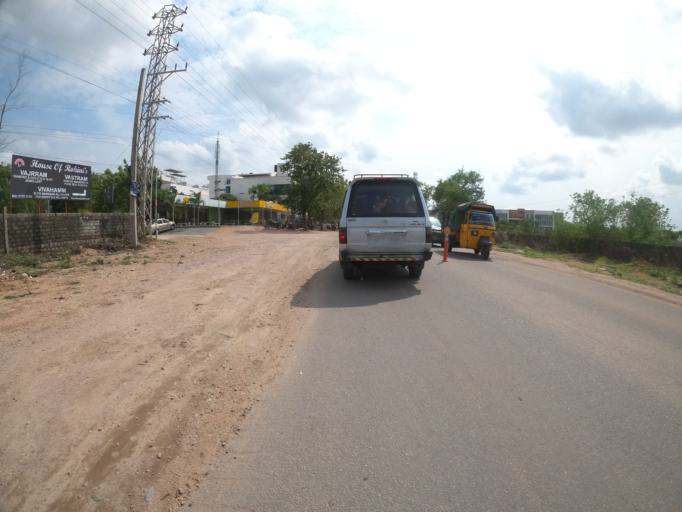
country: IN
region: Telangana
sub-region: Medak
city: Serilingampalle
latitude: 17.3865
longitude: 78.3368
